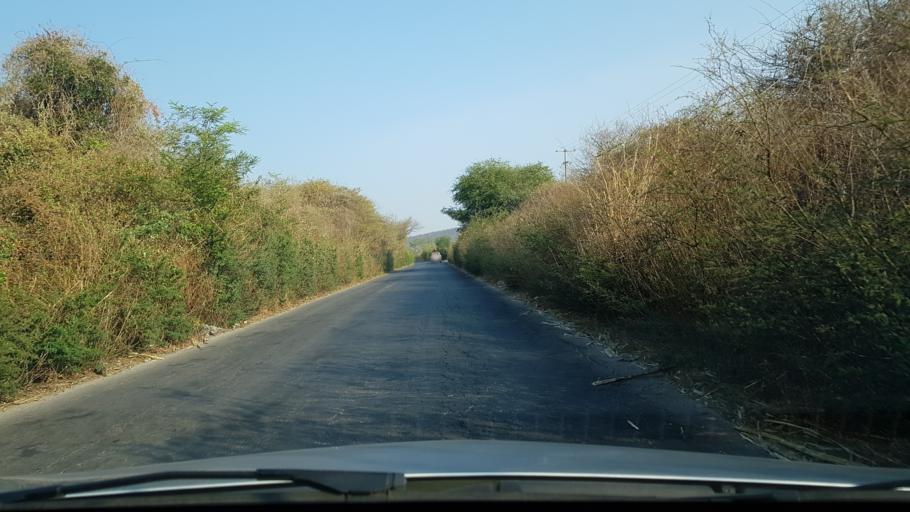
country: MX
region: Morelos
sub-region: Tepalcingo
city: Zacapalco
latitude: 18.6500
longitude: -99.0289
